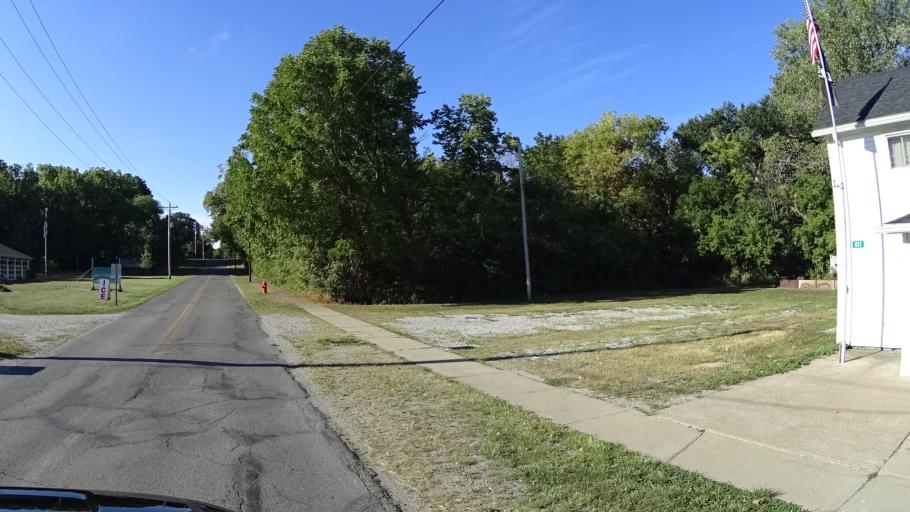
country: US
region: Ohio
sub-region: Erie County
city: Sandusky
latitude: 41.6082
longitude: -82.7082
